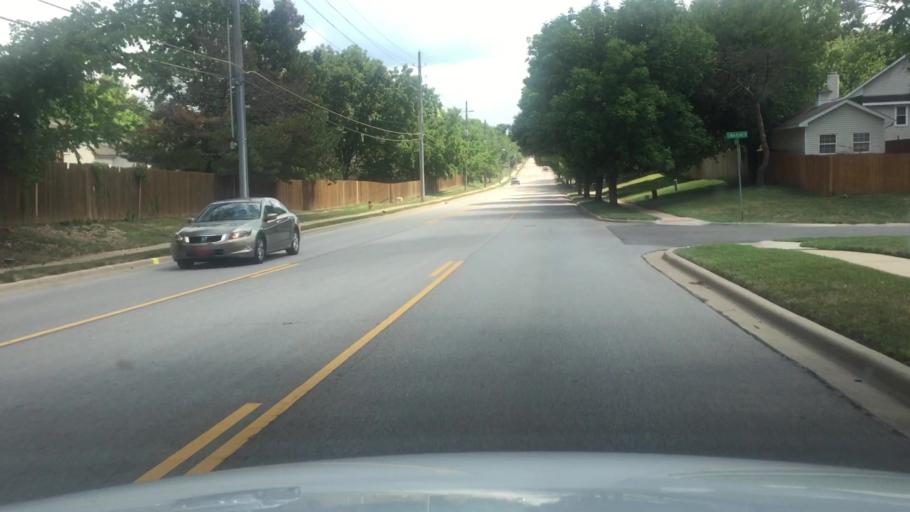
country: US
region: Kansas
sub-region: Johnson County
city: Lenexa
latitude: 38.9620
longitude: -94.7610
